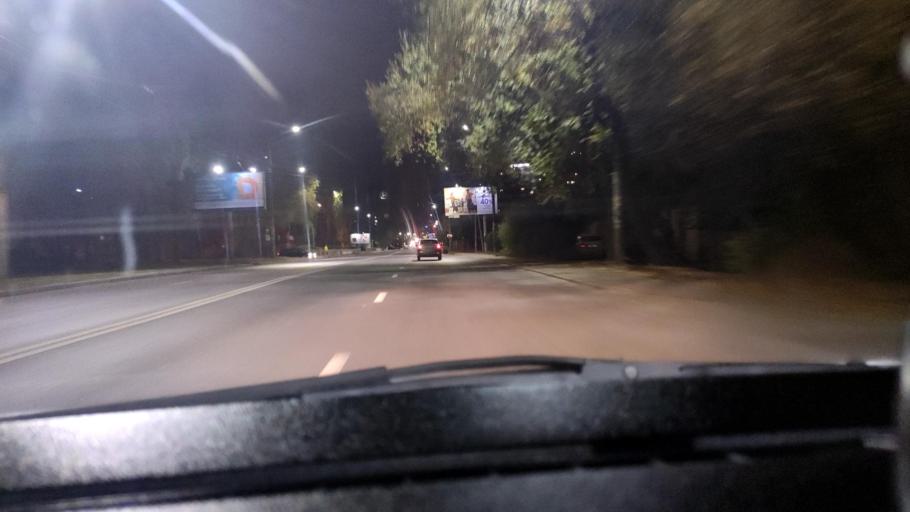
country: RU
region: Voronezj
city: Podgornoye
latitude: 51.7016
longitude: 39.1575
